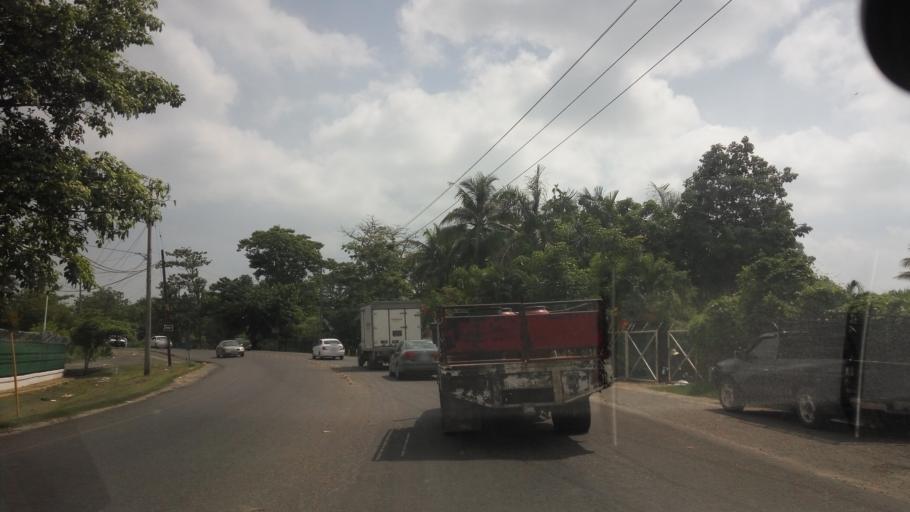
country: MX
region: Chiapas
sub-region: Reforma
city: El Carmen (El Limon)
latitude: 17.8858
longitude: -93.1442
